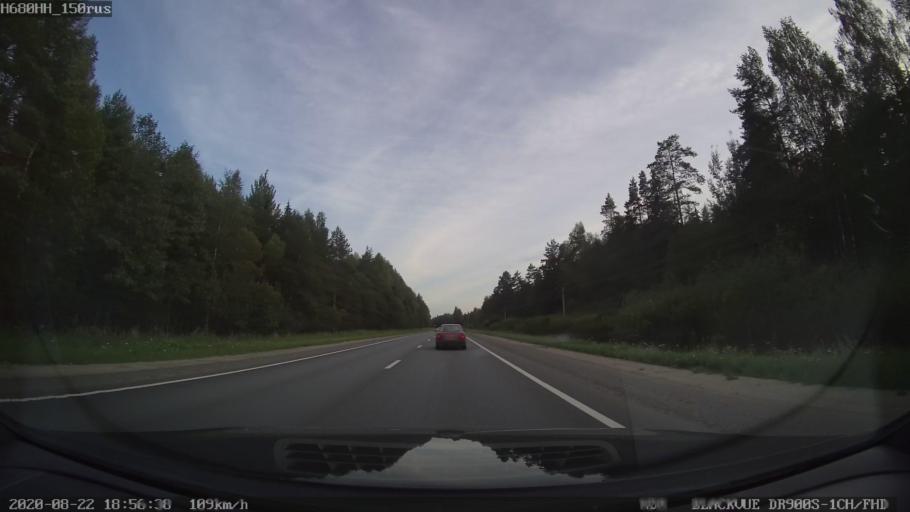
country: RU
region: Tverskaya
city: Rameshki
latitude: 57.1802
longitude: 36.0809
